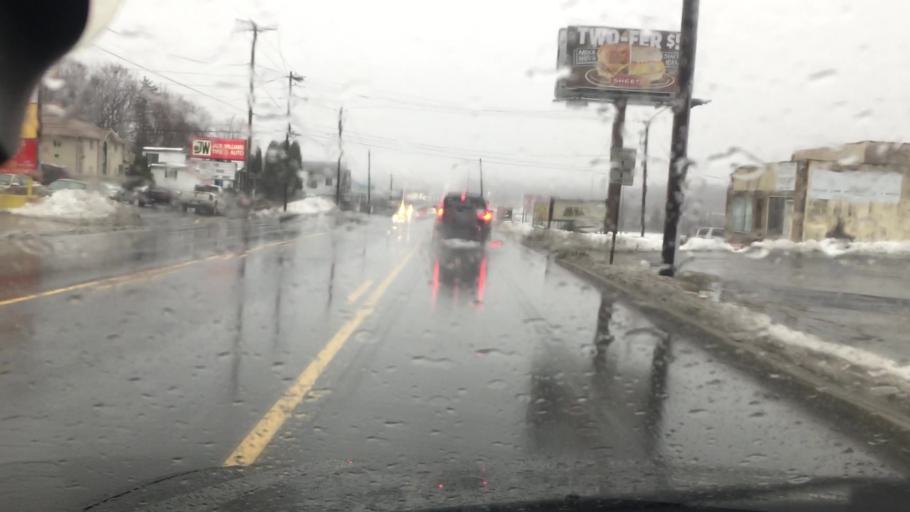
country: US
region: Pennsylvania
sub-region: Luzerne County
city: Harleigh
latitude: 40.9740
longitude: -75.9782
